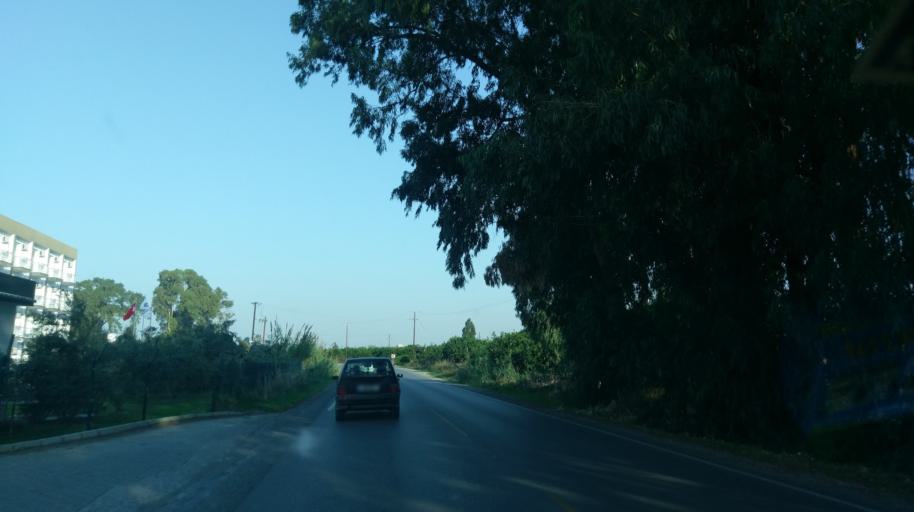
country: CY
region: Lefkosia
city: Lefka
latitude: 35.1573
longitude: 32.8949
